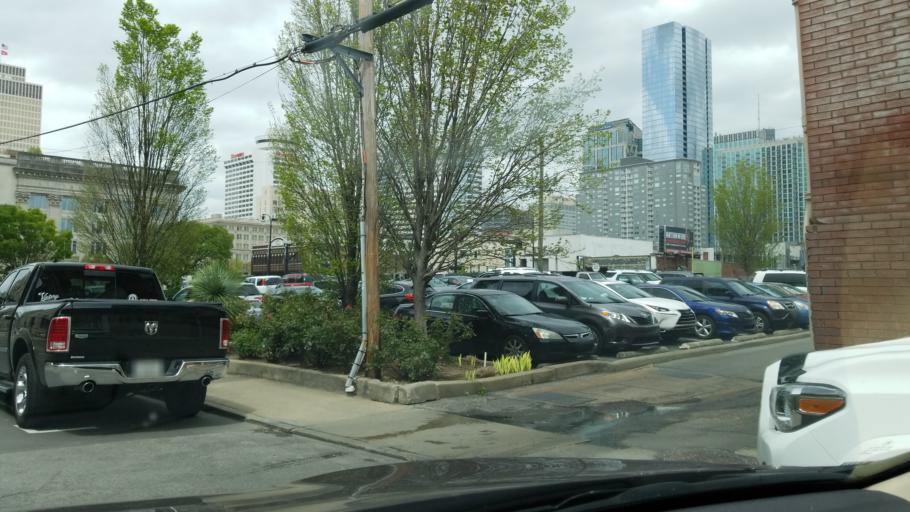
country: US
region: Tennessee
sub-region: Davidson County
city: Nashville
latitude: 36.1593
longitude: -86.7831
